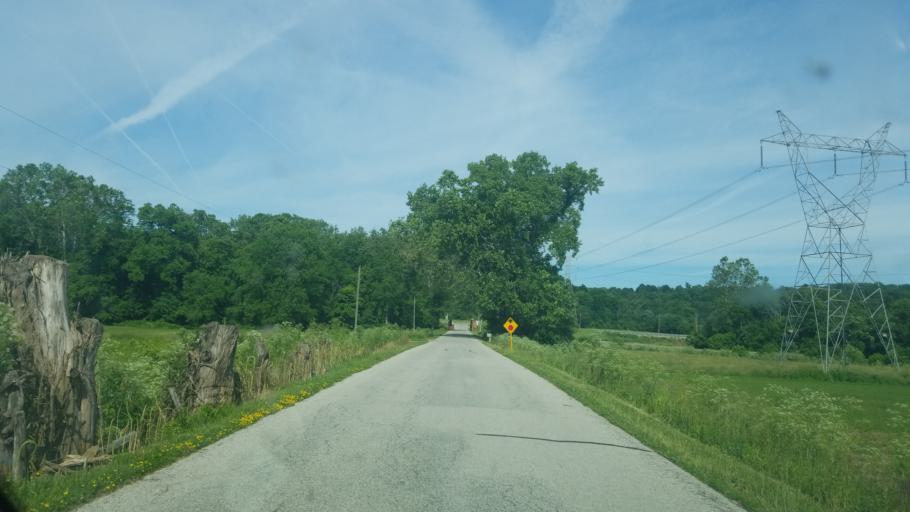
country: US
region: Ohio
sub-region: Licking County
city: Utica
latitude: 40.2093
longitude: -82.4402
